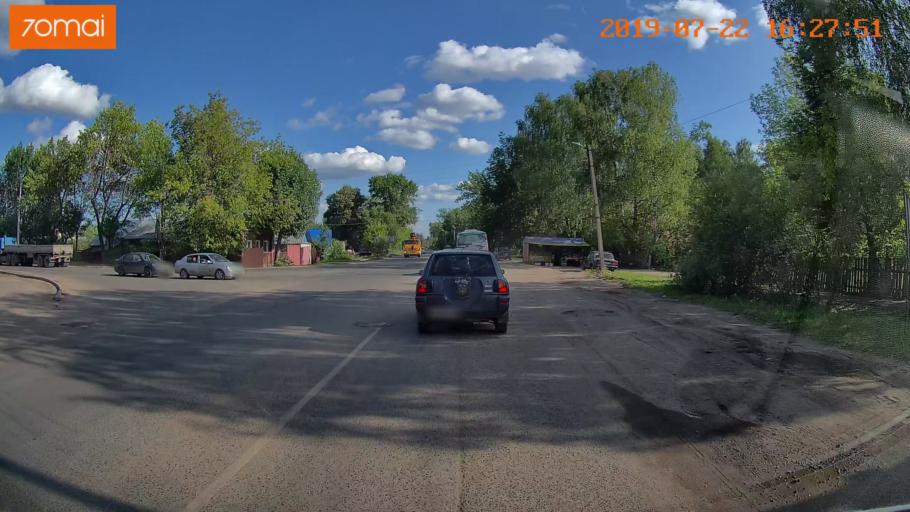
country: RU
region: Ivanovo
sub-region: Gorod Ivanovo
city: Ivanovo
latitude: 57.0418
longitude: 40.9475
